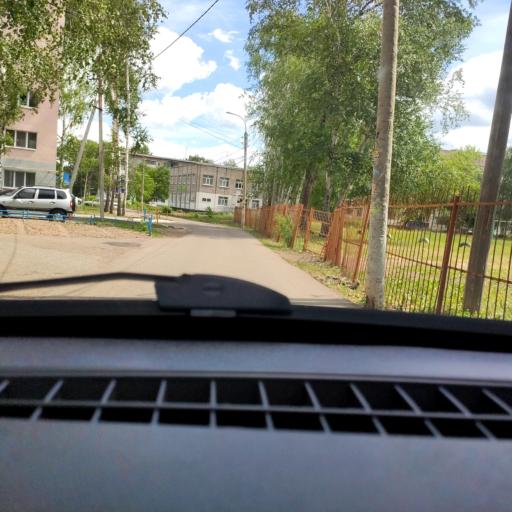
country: RU
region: Bashkortostan
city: Sterlitamak
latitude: 53.6362
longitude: 55.9299
